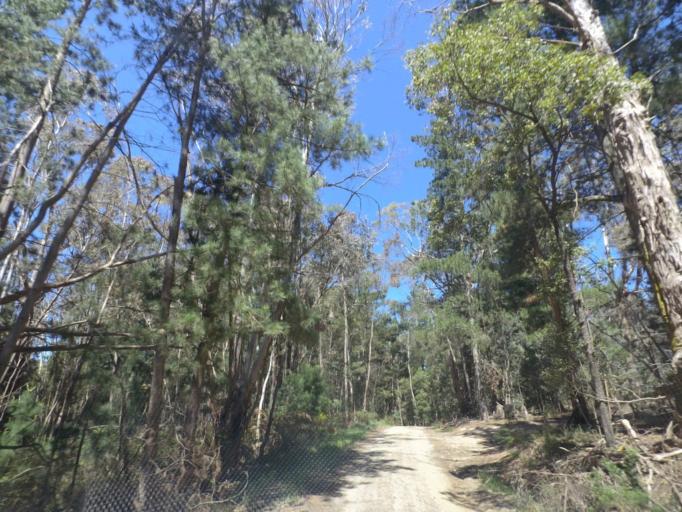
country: AU
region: Victoria
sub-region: Hume
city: Sunbury
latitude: -37.3912
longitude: 144.5534
